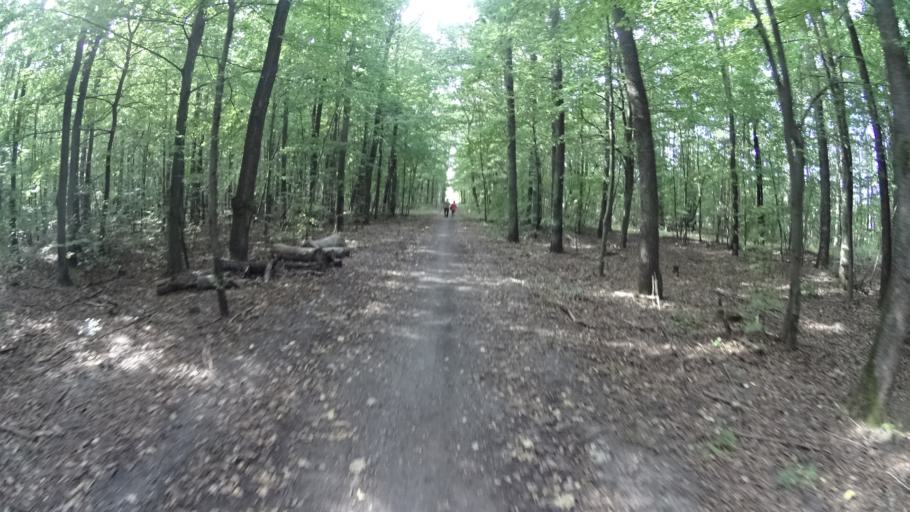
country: PL
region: Masovian Voivodeship
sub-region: Powiat warszawski zachodni
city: Babice
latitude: 52.2742
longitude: 20.8683
